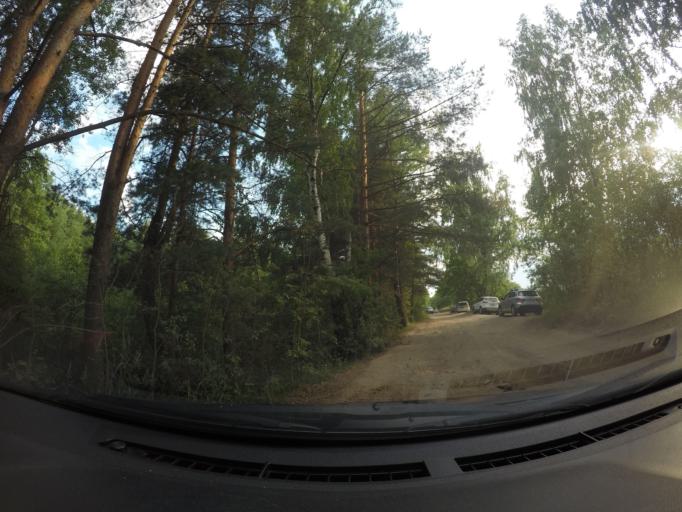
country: RU
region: Moskovskaya
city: Krasnyy Tkach
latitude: 55.4168
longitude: 39.2295
